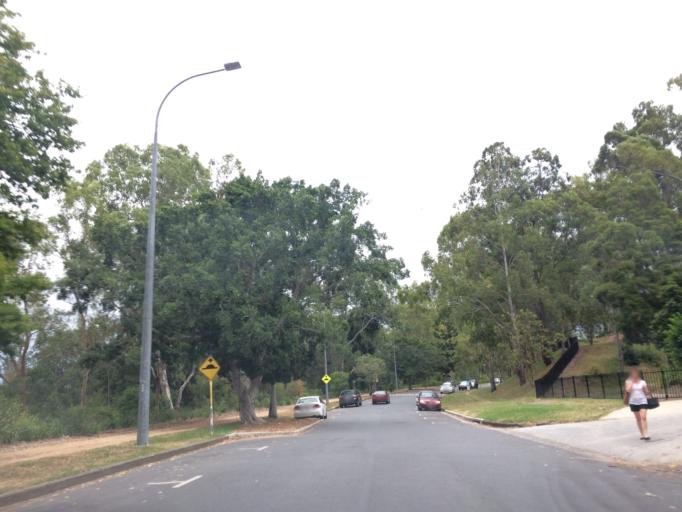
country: AU
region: Queensland
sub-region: Brisbane
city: Yeronga
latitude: -27.5026
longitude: 153.0139
